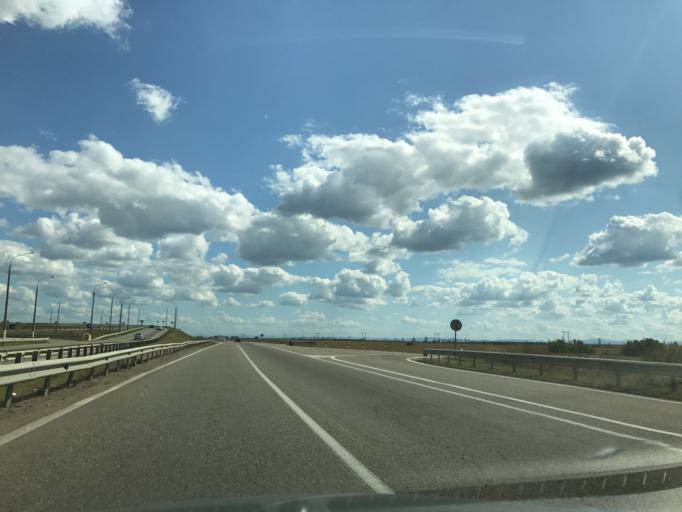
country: RU
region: Adygeya
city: Adygeysk
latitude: 44.8958
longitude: 39.1647
